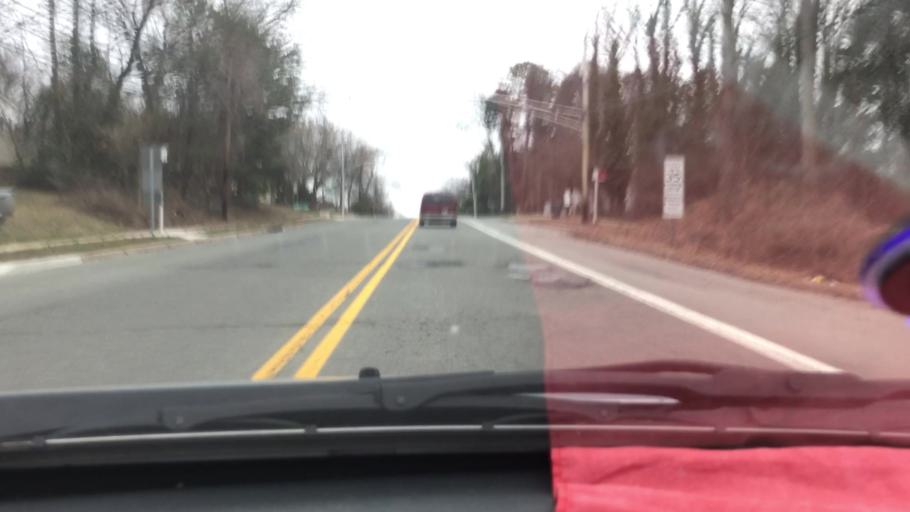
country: US
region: Maryland
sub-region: Prince George's County
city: Lanham
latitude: 38.9735
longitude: -76.8661
